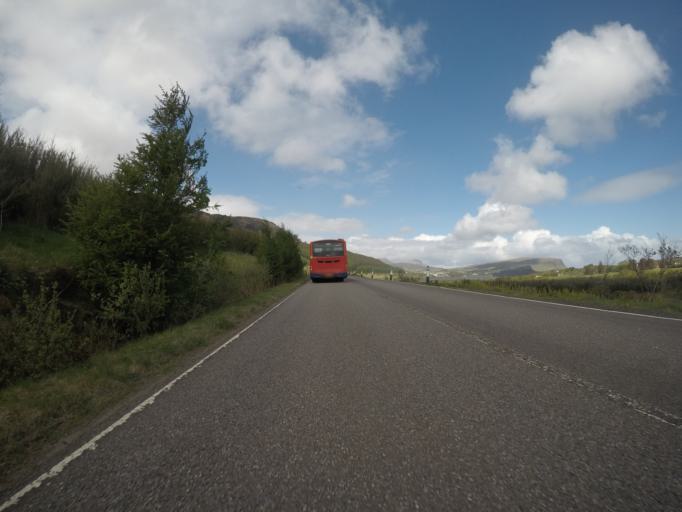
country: GB
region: Scotland
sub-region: Highland
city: Portree
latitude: 57.3840
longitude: -6.2021
